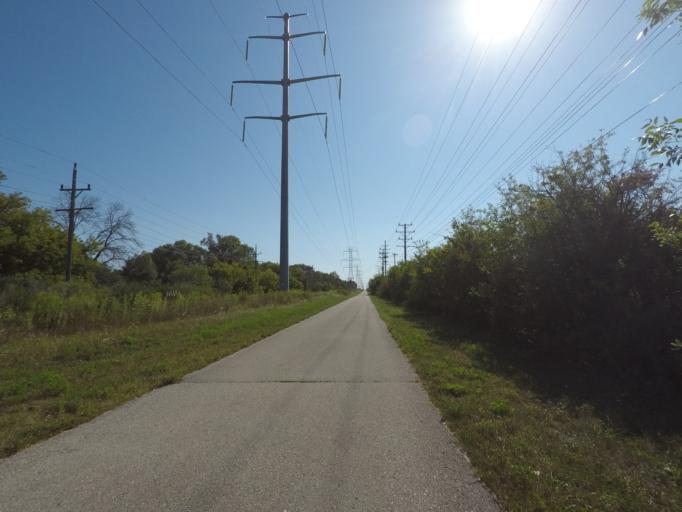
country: US
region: Wisconsin
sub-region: Waukesha County
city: New Berlin
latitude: 43.0101
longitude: -88.1158
